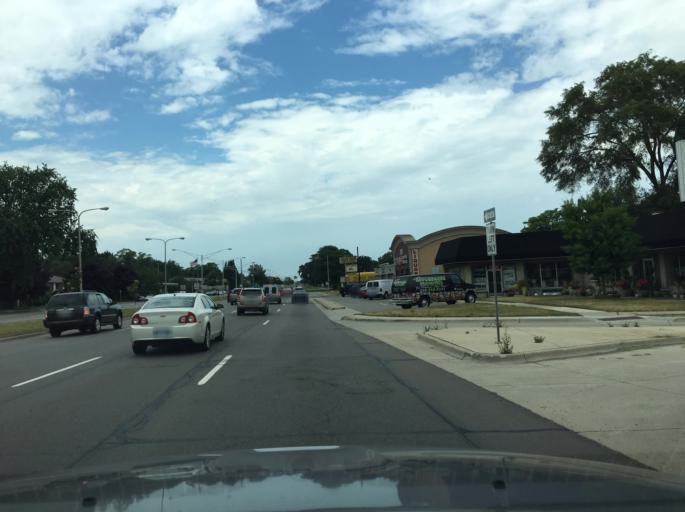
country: US
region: Michigan
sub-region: Oakland County
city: Royal Oak
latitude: 42.4813
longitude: -83.1509
